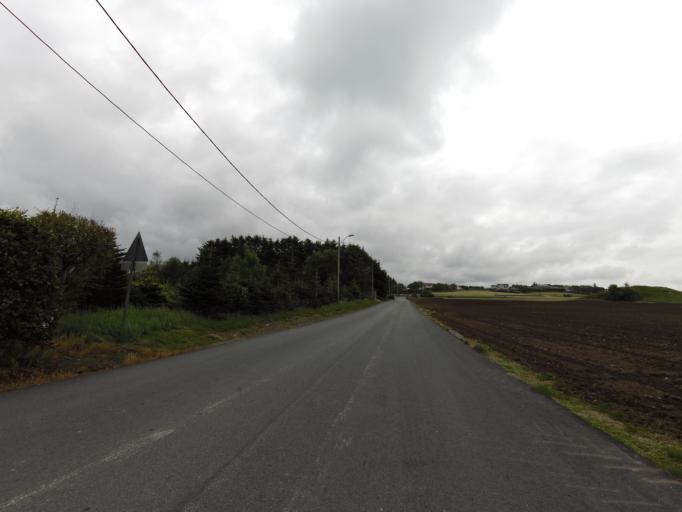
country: NO
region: Rogaland
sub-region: Klepp
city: Kleppe
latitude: 58.8348
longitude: 5.5952
